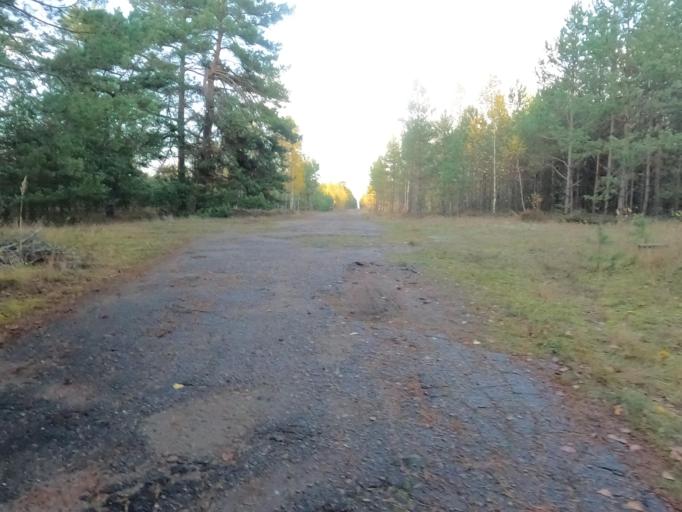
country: PL
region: West Pomeranian Voivodeship
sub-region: Powiat szczecinecki
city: Borne Sulinowo
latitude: 53.5475
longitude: 16.5199
